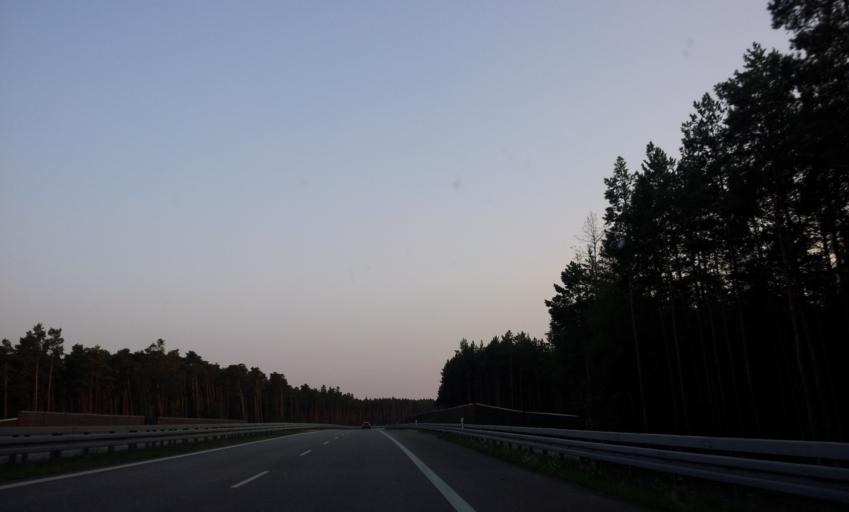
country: DE
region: Brandenburg
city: Trebbin
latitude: 52.1402
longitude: 13.2305
